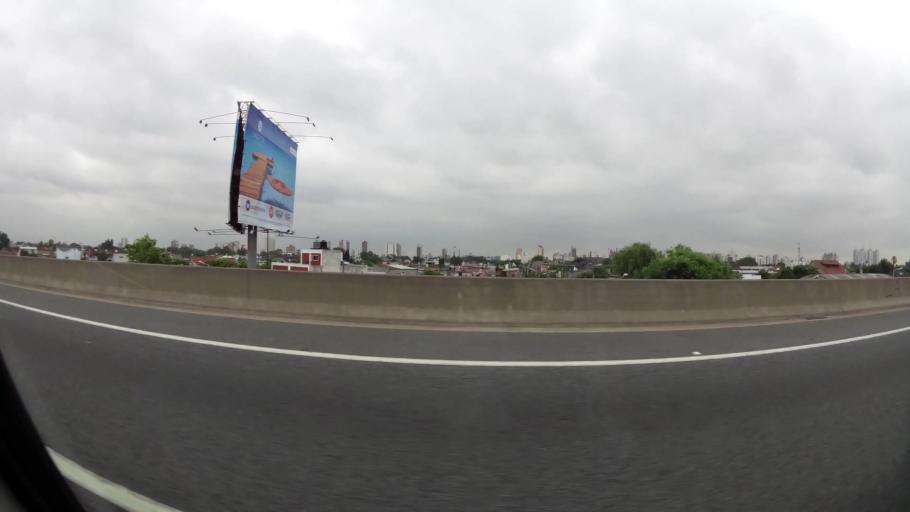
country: AR
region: Buenos Aires
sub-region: Partido de Avellaneda
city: Avellaneda
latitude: -34.6612
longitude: -58.3478
